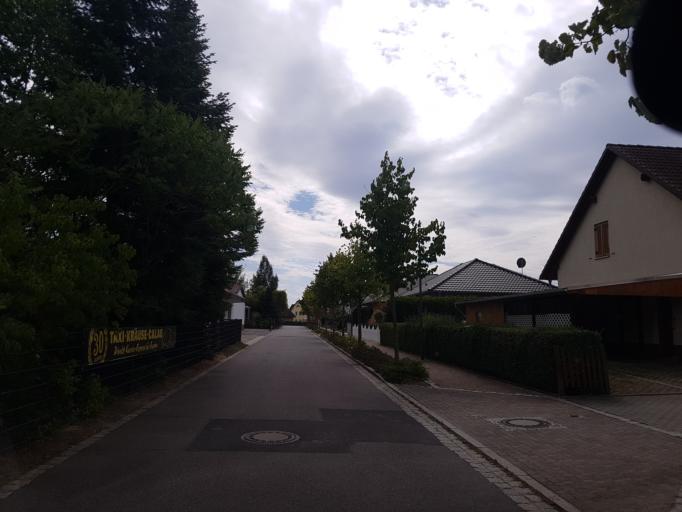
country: DE
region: Brandenburg
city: Calau
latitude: 51.7428
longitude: 13.9444
